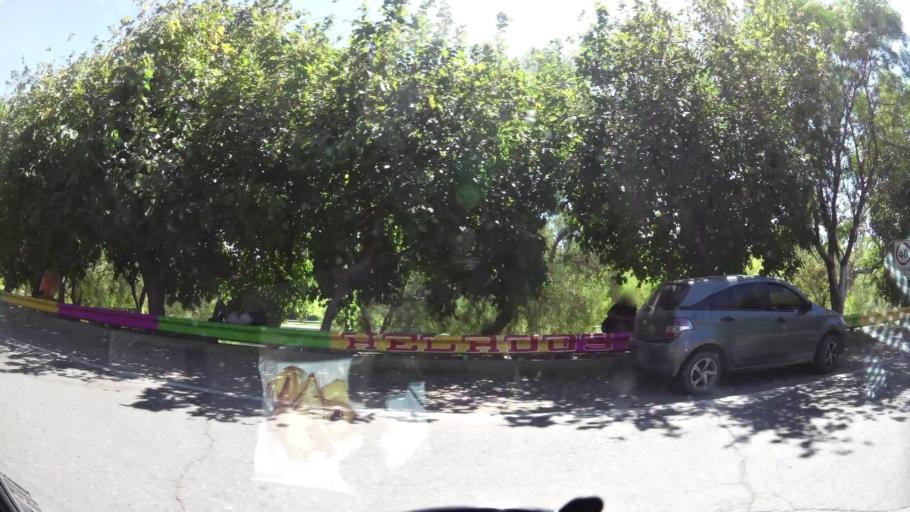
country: AR
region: San Juan
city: San Juan
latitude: -31.5172
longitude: -68.5284
